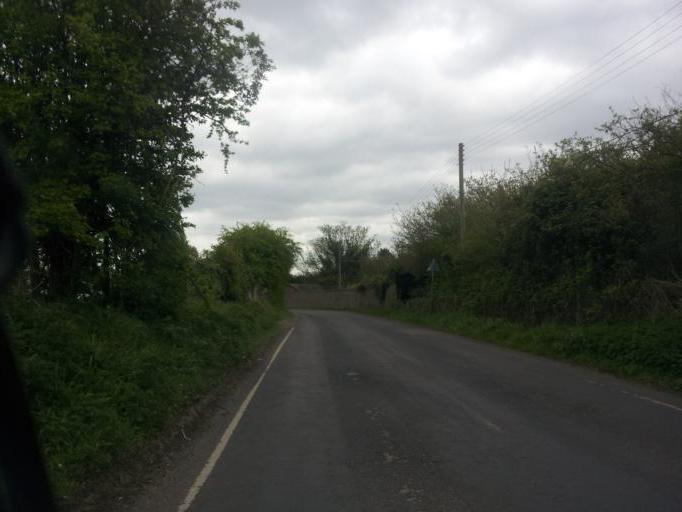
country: GB
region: England
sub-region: Kent
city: Newington
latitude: 51.3753
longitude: 0.6732
